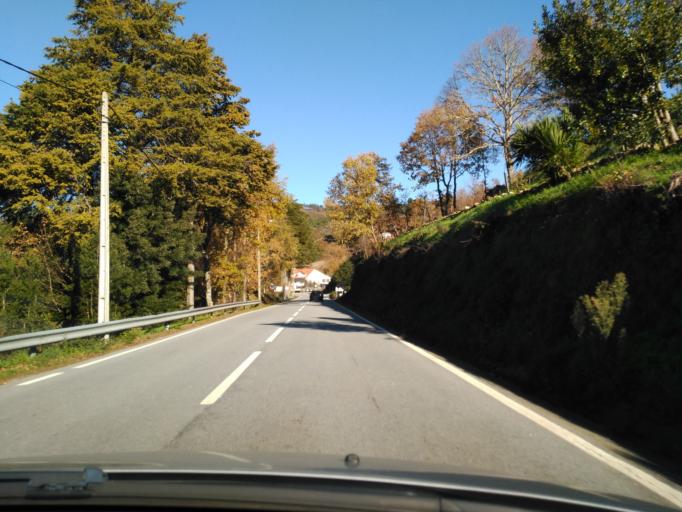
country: PT
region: Braga
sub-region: Cabeceiras de Basto
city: Cabeceiras de Basto
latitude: 41.6776
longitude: -7.9508
